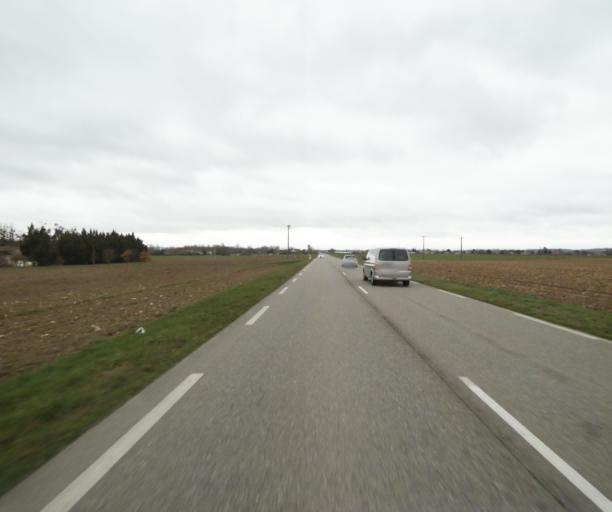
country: FR
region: Midi-Pyrenees
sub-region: Departement de l'Ariege
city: Pamiers
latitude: 43.1775
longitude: 1.6066
